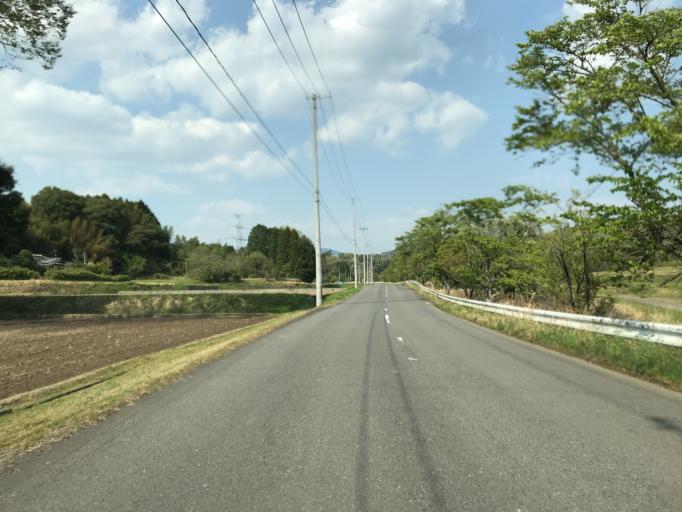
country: JP
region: Fukushima
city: Iwaki
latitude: 36.9628
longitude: 140.7546
